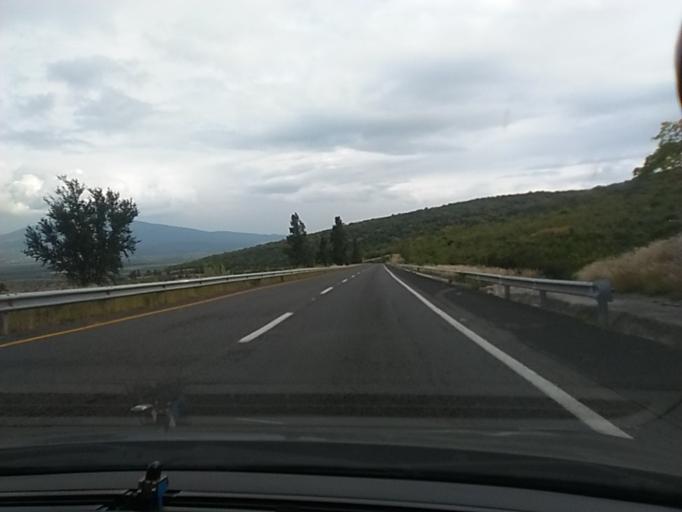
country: MX
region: Michoacan
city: Ixtlan
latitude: 20.1988
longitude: -102.3208
